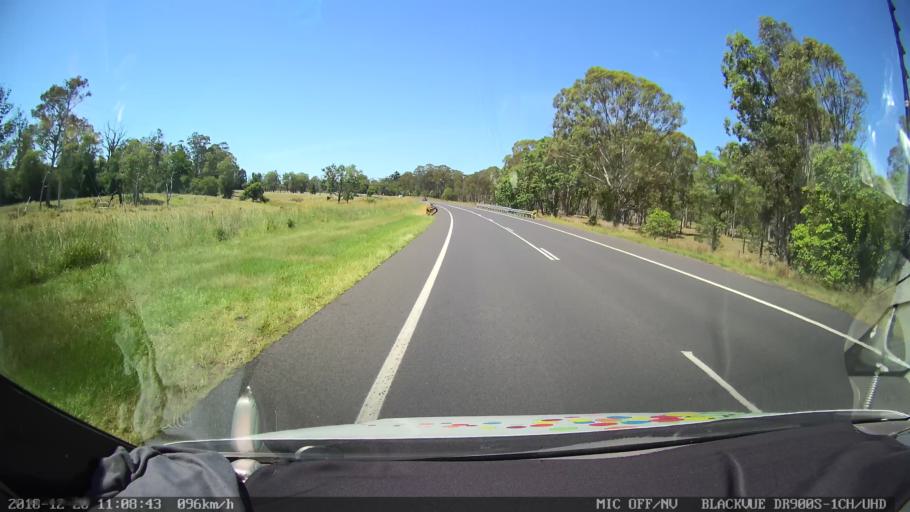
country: AU
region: New South Wales
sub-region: Richmond Valley
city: Casino
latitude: -28.9260
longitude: 153.0048
